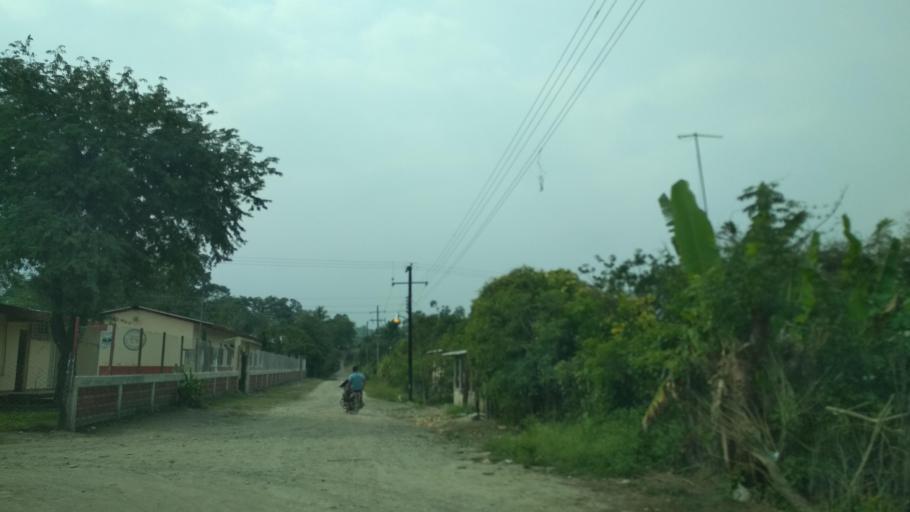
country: MM
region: Kayah
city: Loikaw
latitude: 20.2123
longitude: 97.3014
